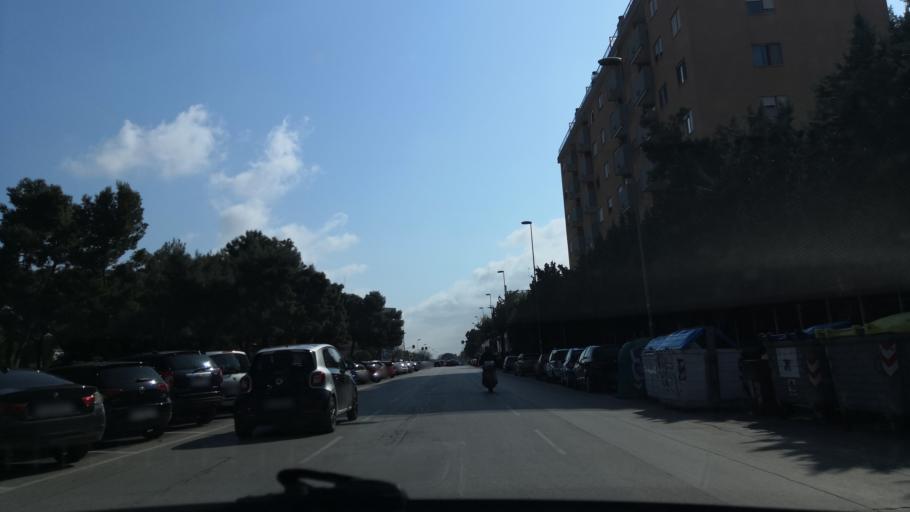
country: IT
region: Apulia
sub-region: Provincia di Bari
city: Bari
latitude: 41.1026
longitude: 16.8736
